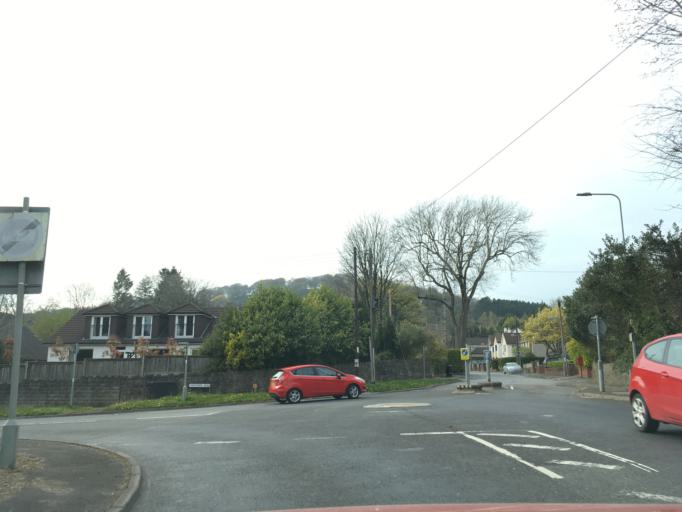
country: GB
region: Wales
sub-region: Cardiff
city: Radyr
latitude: 51.5309
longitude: -3.2242
